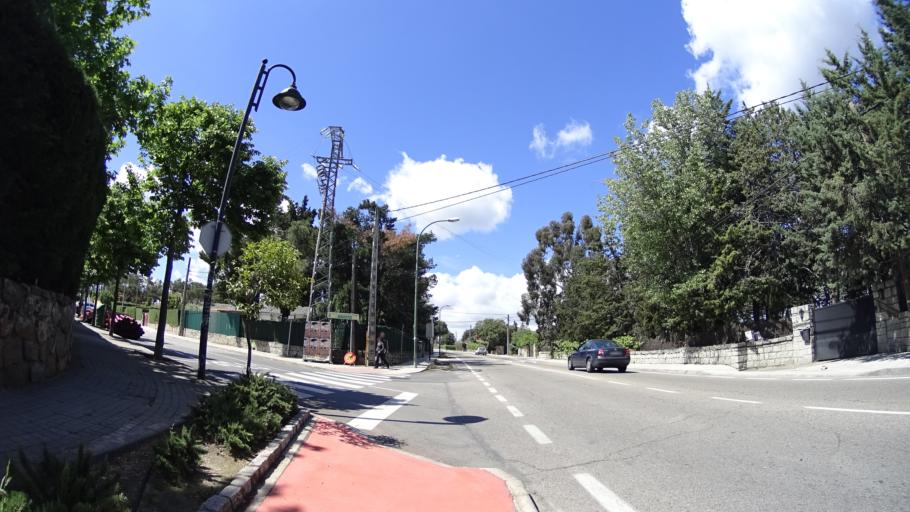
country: ES
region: Madrid
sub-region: Provincia de Madrid
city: Galapagar
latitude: 40.5721
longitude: -4.0079
